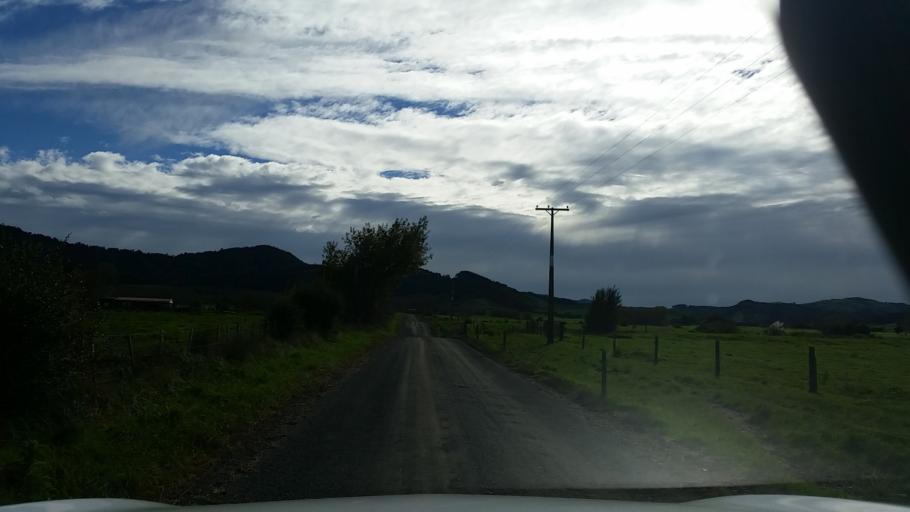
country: NZ
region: Waikato
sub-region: Hauraki District
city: Ngatea
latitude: -37.5123
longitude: 175.4090
